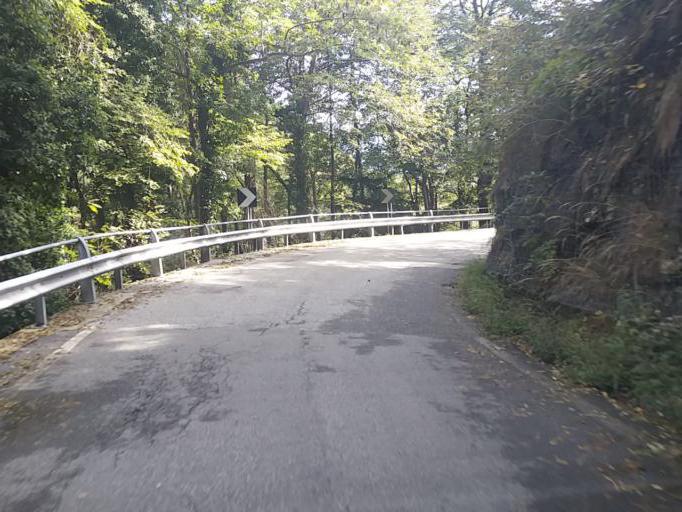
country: IT
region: Piedmont
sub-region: Provincia Verbano-Cusio-Ossola
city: Trarego
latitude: 46.0626
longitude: 8.6668
